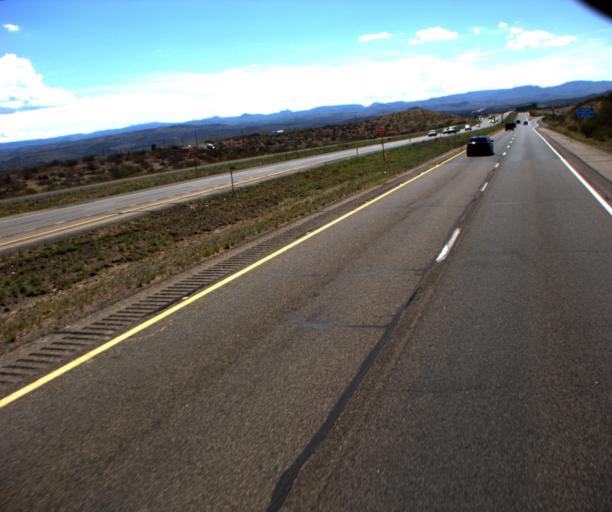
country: US
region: Arizona
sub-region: Yavapai County
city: Spring Valley
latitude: 34.3381
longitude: -112.1329
